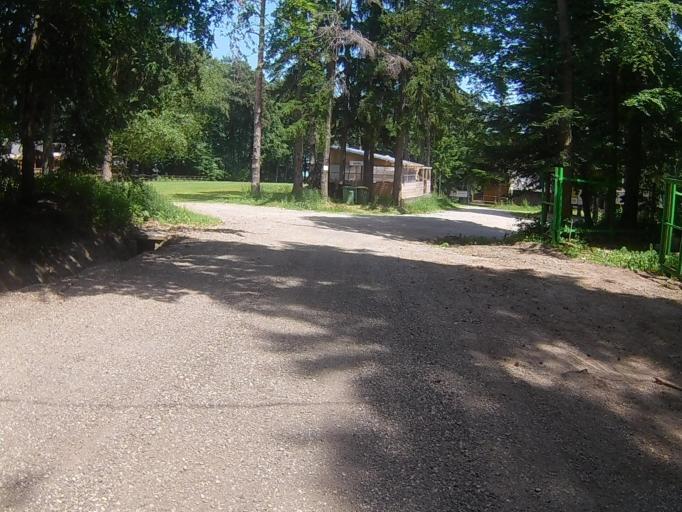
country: SI
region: Maribor
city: Pekre
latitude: 46.5144
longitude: 15.5825
